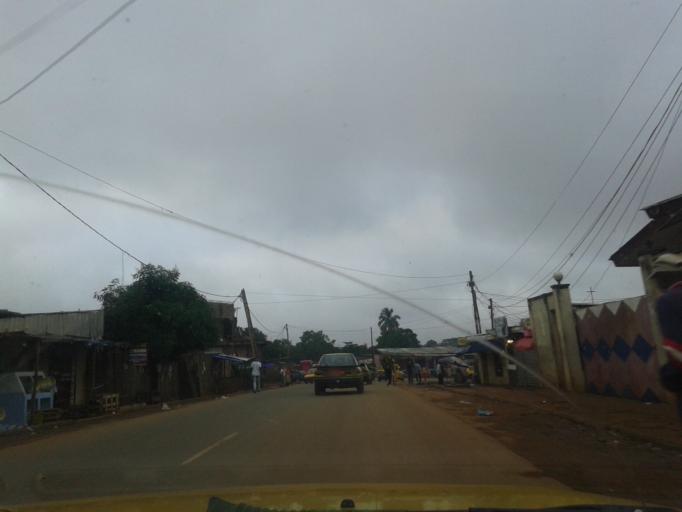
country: CM
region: Centre
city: Yaounde
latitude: 3.8861
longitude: 11.5304
